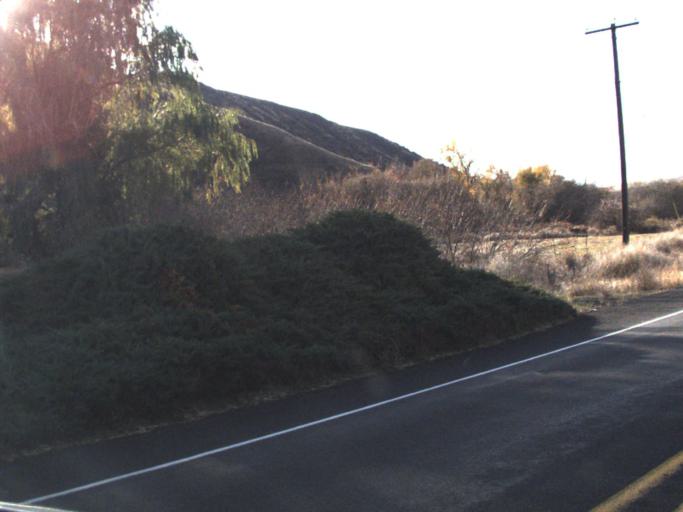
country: US
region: Washington
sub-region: Walla Walla County
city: Waitsburg
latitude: 46.2895
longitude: -118.0834
